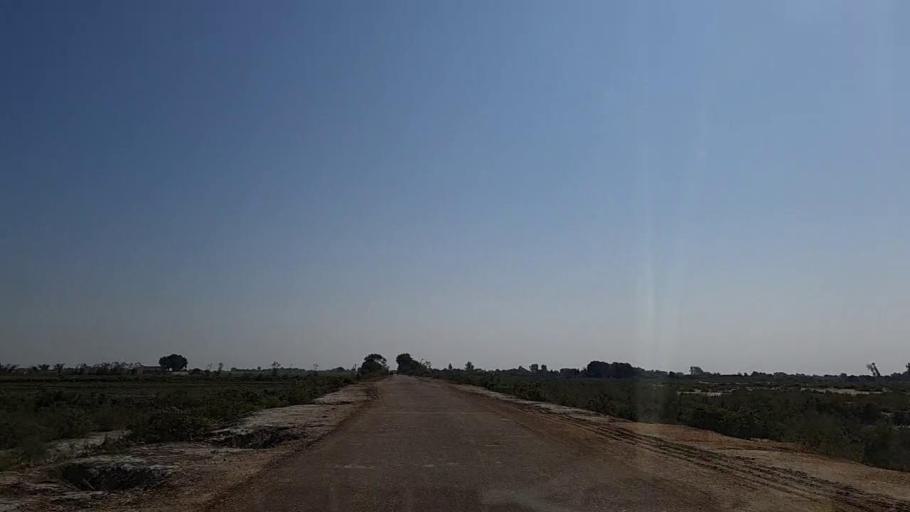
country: PK
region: Sindh
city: Chuhar Jamali
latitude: 24.5262
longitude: 68.0848
